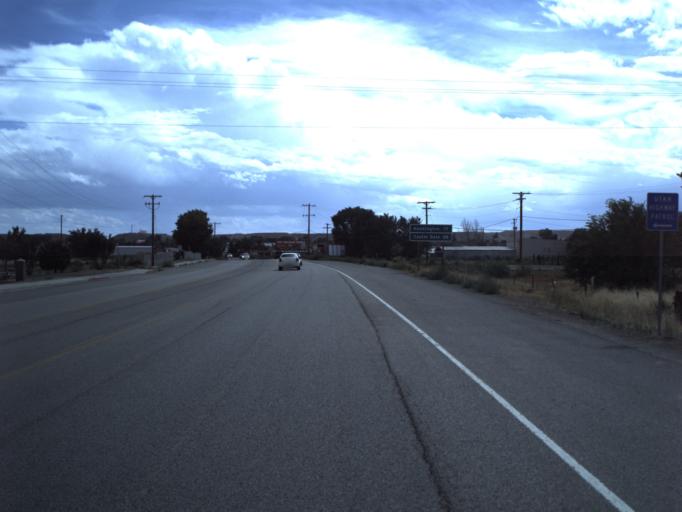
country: US
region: Utah
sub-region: Carbon County
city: Price
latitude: 39.5810
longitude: -110.8155
